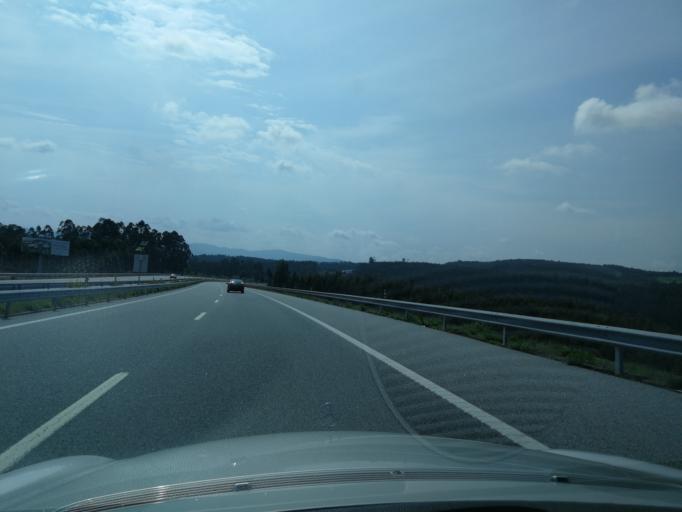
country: PT
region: Braga
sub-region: Vila Nova de Famalicao
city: Calendario
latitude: 41.3834
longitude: -8.5460
